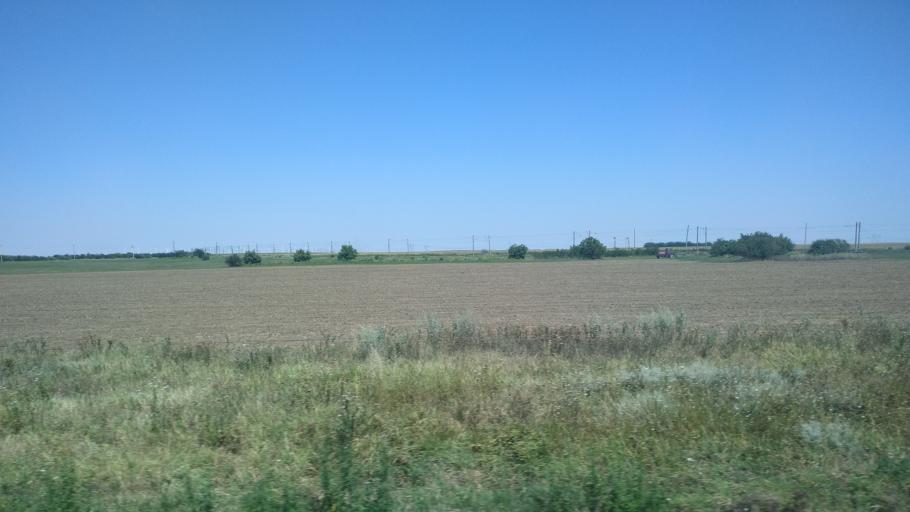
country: RO
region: Ialomita
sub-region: Municipiul Fetesti
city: Fetesti-Gara
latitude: 44.4177
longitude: 27.8023
